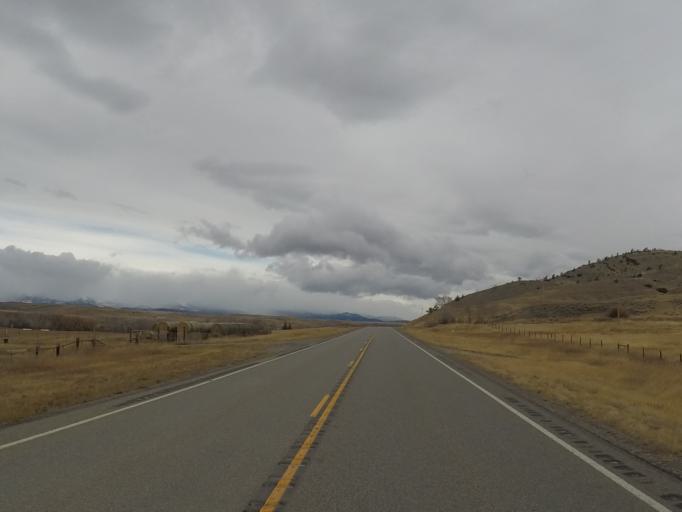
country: US
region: Montana
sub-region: Sweet Grass County
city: Big Timber
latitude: 45.8762
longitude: -109.9509
